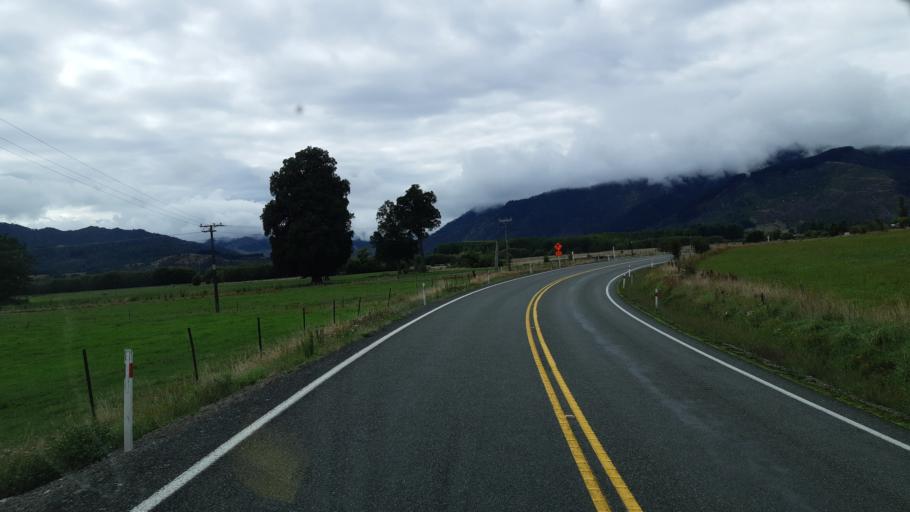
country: NZ
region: West Coast
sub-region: Buller District
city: Westport
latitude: -41.7947
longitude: 172.3065
